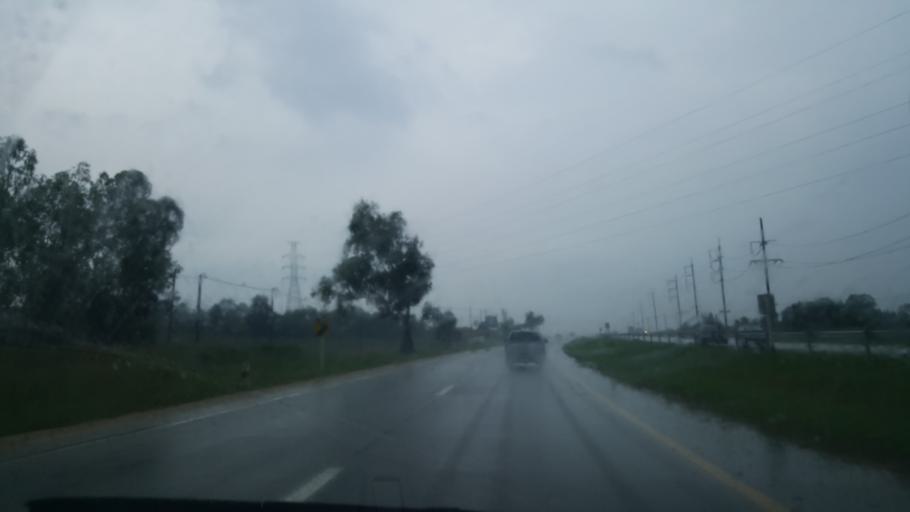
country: TH
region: Chon Buri
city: Ban Talat Bueng
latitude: 12.9299
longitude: 101.0361
